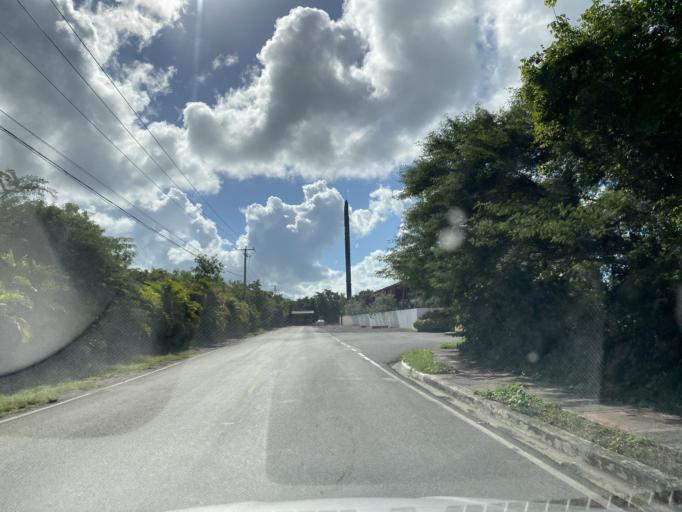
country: DO
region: La Altagracia
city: San Rafael del Yuma
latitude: 18.3343
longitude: -68.8087
